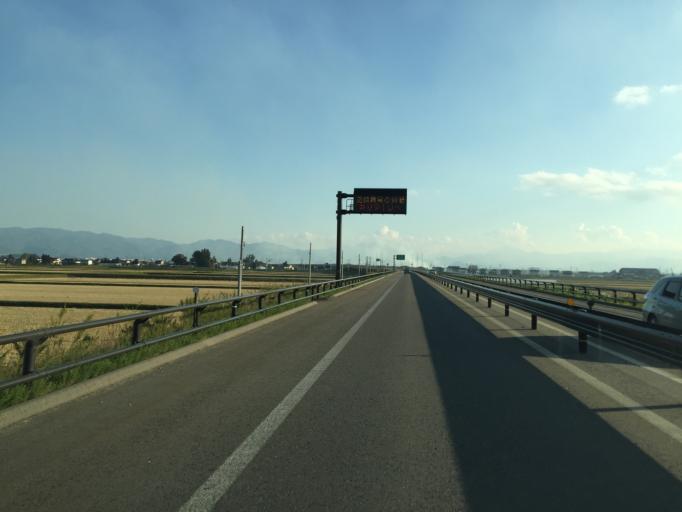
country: JP
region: Fukushima
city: Kitakata
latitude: 37.5614
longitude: 139.8954
